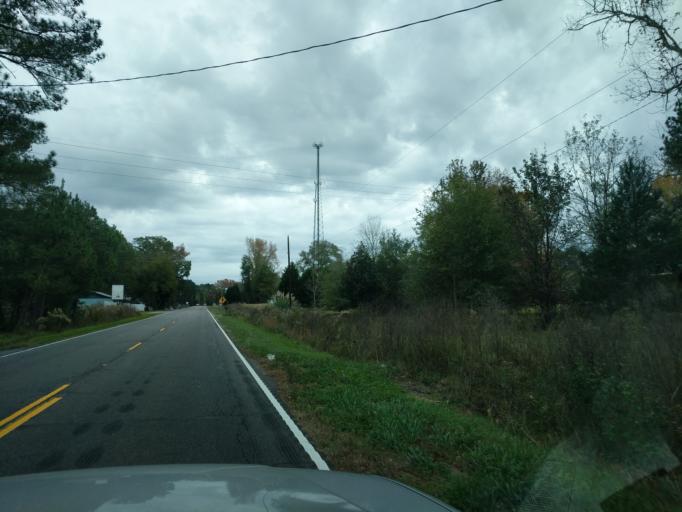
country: US
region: South Carolina
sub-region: Lexington County
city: Batesburg
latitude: 33.9212
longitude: -81.5791
